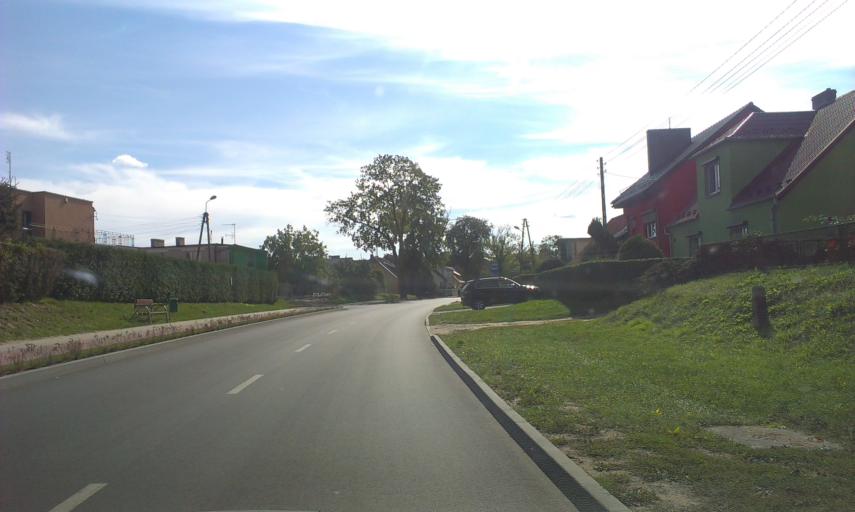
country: PL
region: Greater Poland Voivodeship
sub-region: Powiat pilski
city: Lobzenica
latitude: 53.2668
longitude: 17.2574
